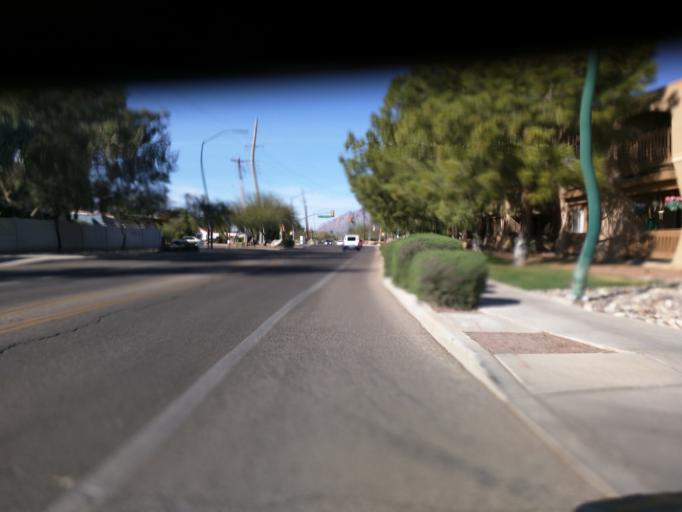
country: US
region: Arizona
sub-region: Pima County
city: Catalina Foothills
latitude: 32.2637
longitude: -110.9523
